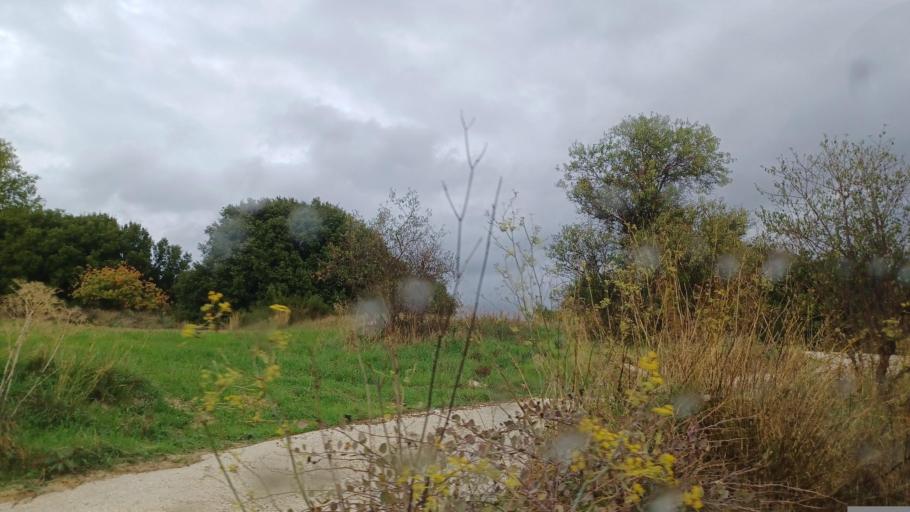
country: CY
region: Pafos
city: Mesogi
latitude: 34.8643
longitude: 32.5402
